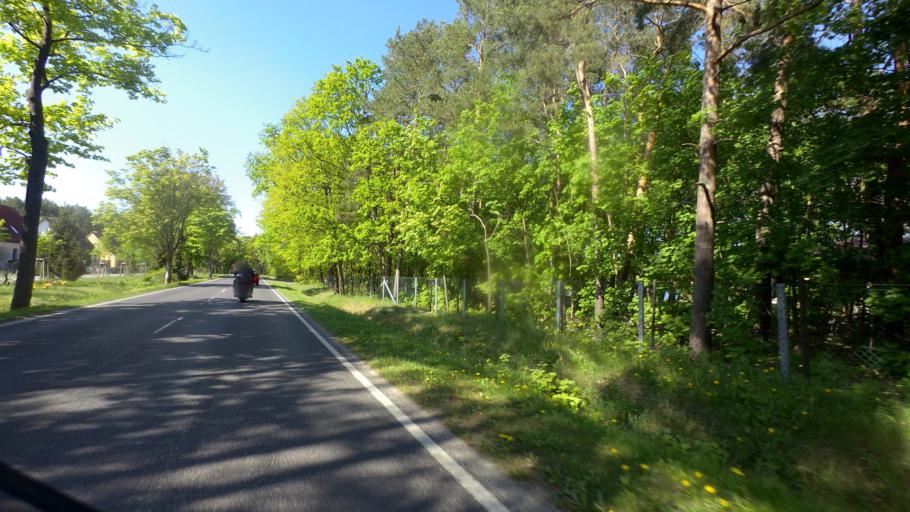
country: DE
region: Brandenburg
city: Bestensee
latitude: 52.2384
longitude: 13.6660
